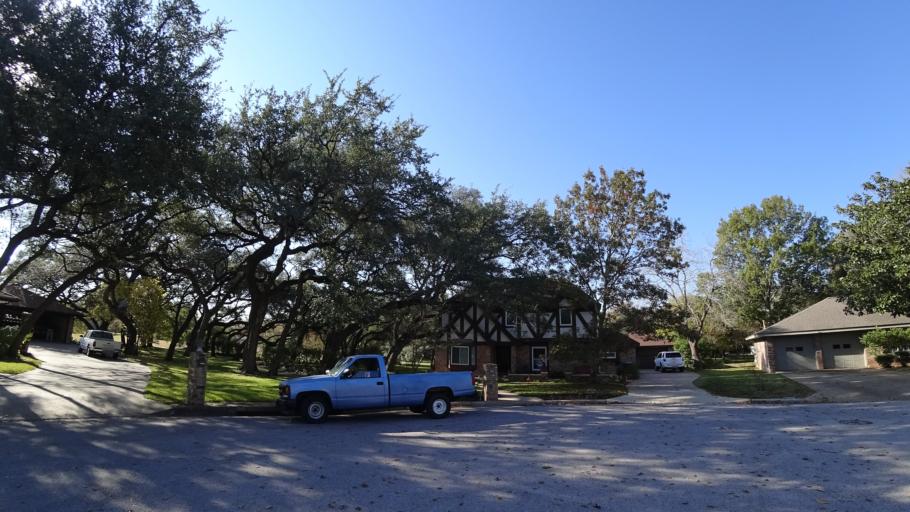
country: US
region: Texas
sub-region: Travis County
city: Shady Hollow
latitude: 30.2202
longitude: -97.8461
